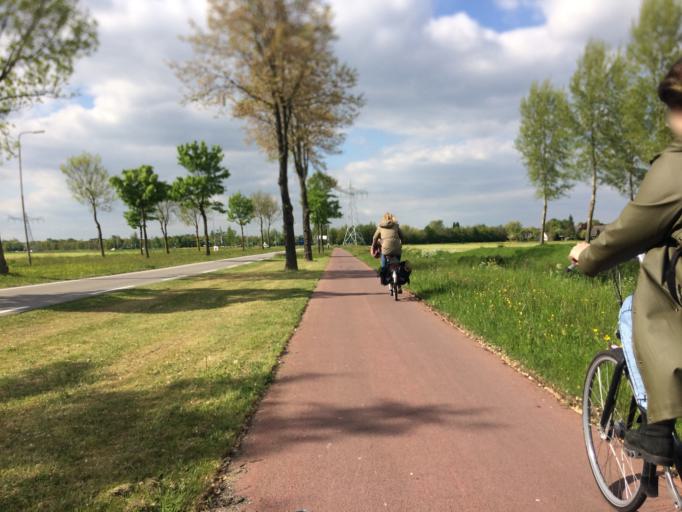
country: NL
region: Gelderland
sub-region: Gemeente Maasdriel
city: Hedel
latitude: 51.7157
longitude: 5.2586
